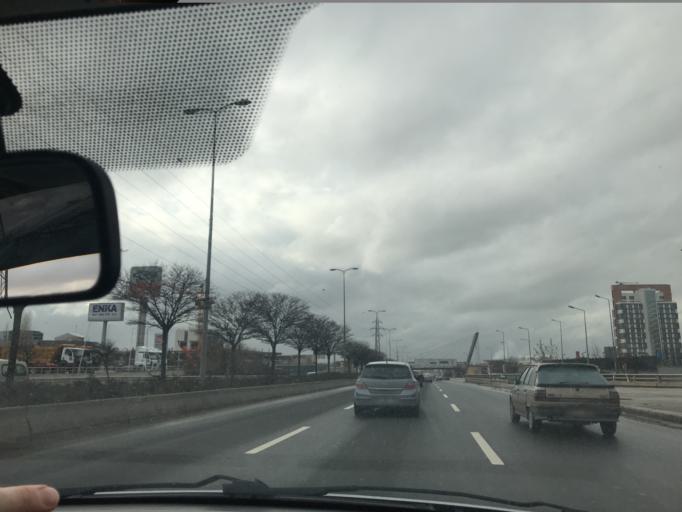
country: TR
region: Ankara
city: Batikent
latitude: 39.9604
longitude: 32.7781
